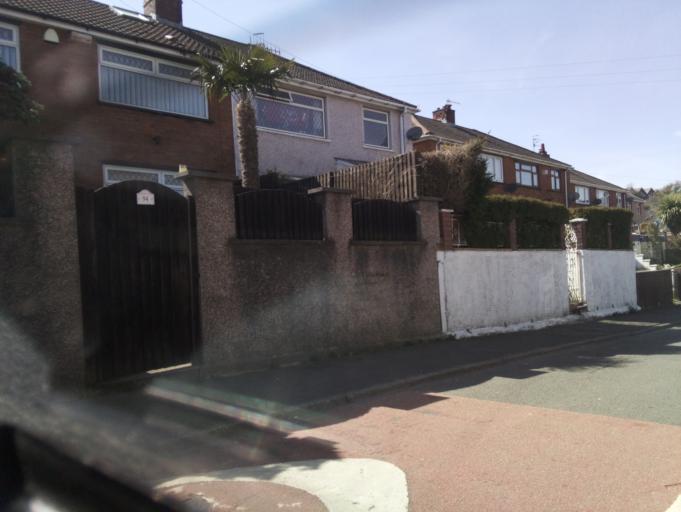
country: GB
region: Wales
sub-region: Rhondda Cynon Taf
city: Mountain Ash
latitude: 51.6770
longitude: -3.3770
